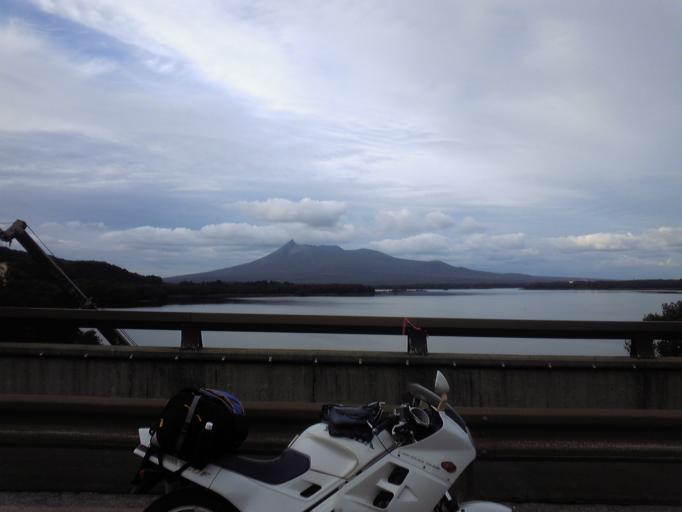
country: JP
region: Hokkaido
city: Nanae
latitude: 41.9561
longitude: 140.6517
